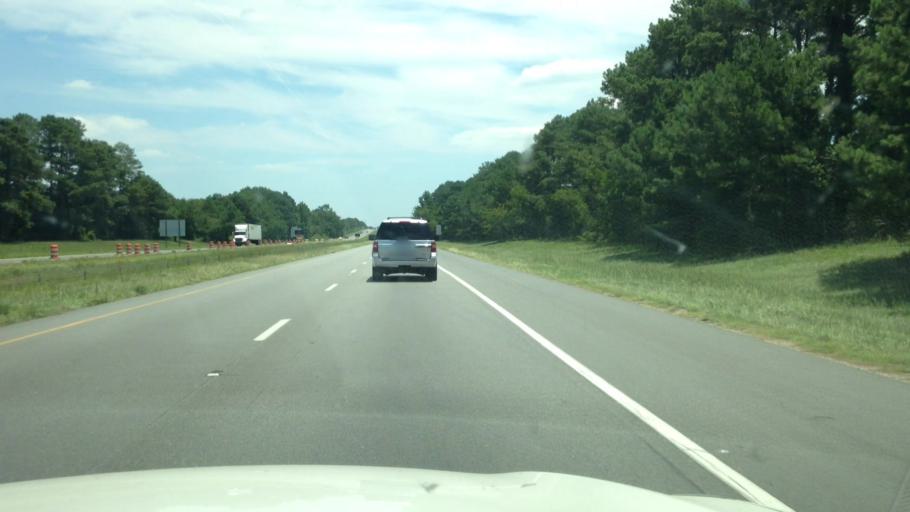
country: US
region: South Carolina
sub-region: Lee County
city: Bishopville
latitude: 34.1926
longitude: -80.2690
